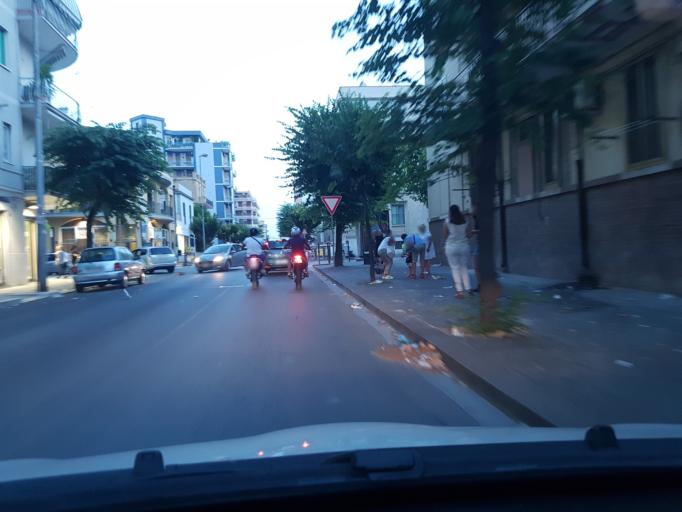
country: IT
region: Apulia
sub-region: Provincia di Foggia
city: Cerignola
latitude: 41.2640
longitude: 15.9084
